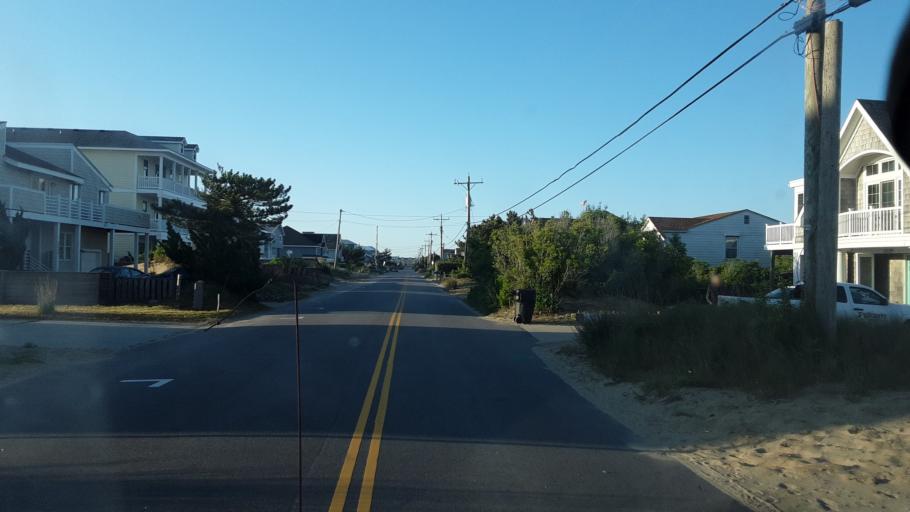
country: US
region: Virginia
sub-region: City of Virginia Beach
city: Virginia Beach
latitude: 36.7117
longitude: -75.9314
